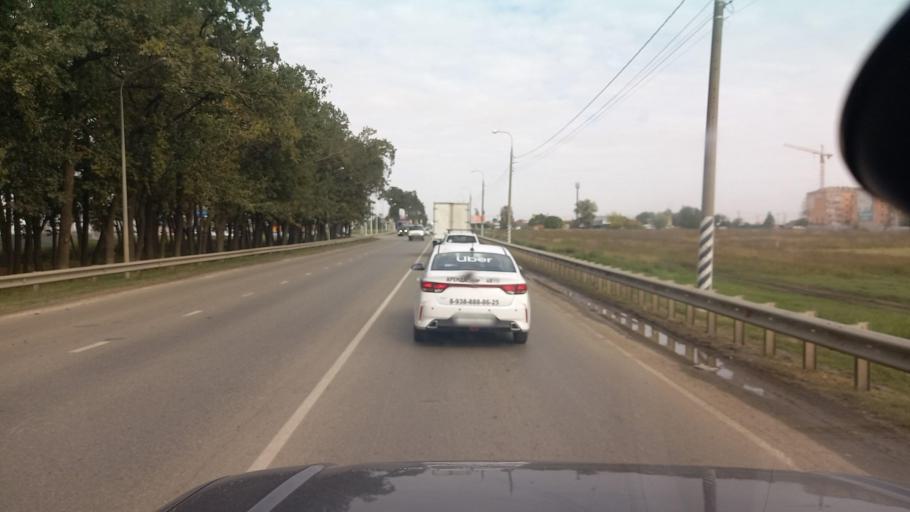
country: RU
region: Krasnodarskiy
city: Krasnodar
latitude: 45.0966
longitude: 38.9110
